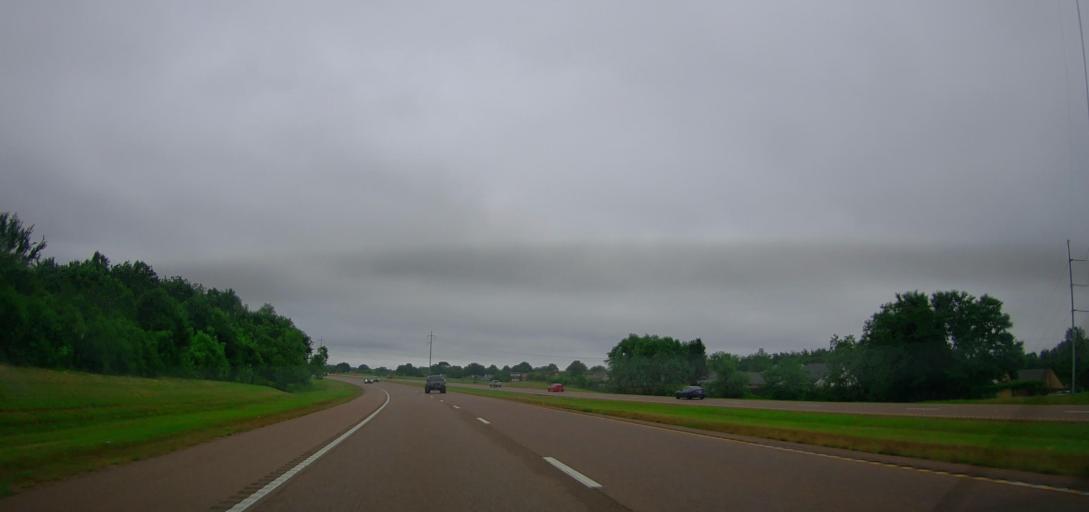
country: US
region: Mississippi
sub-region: De Soto County
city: Olive Branch
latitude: 34.9677
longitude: -89.8044
